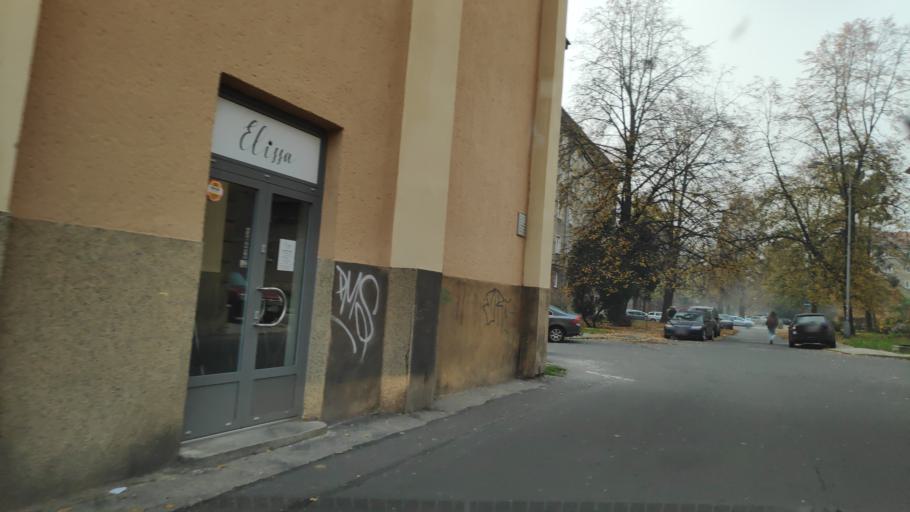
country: CZ
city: Vresina
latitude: 49.8299
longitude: 18.1669
